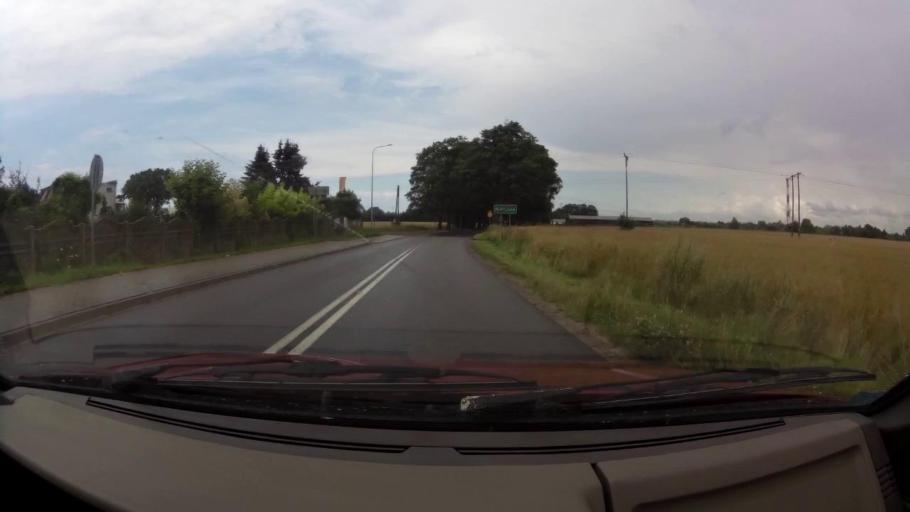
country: PL
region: West Pomeranian Voivodeship
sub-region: Koszalin
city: Koszalin
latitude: 54.1728
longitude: 16.1589
